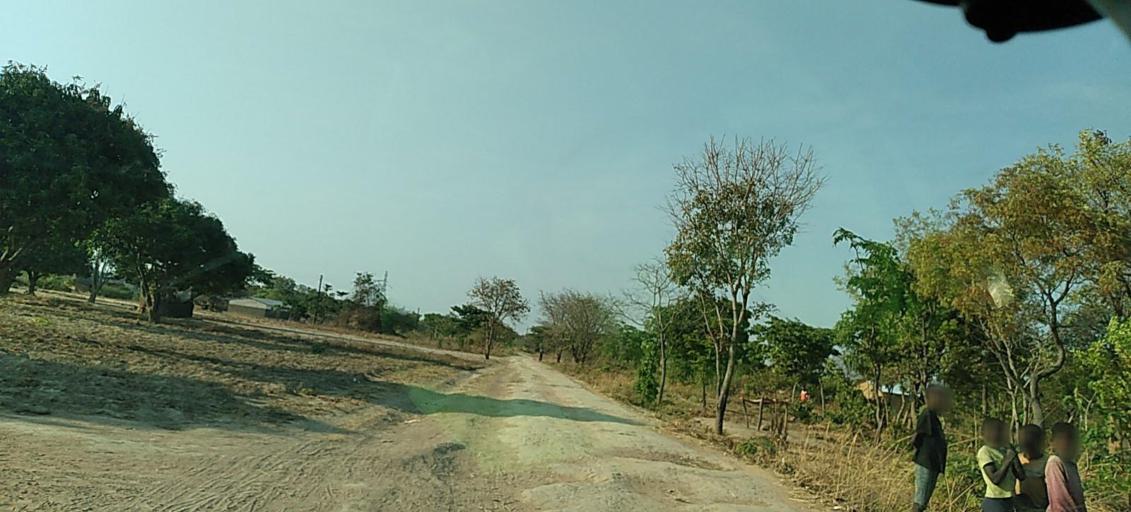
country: ZM
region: North-Western
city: Kalengwa
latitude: -13.1490
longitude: 25.0340
